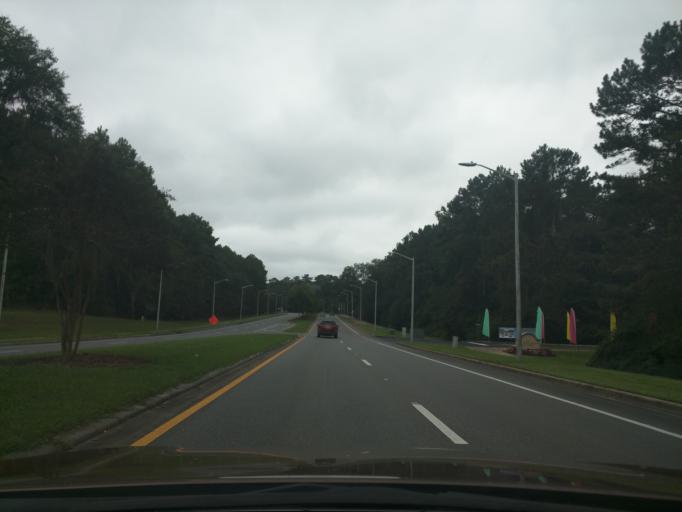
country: US
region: Florida
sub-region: Leon County
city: Tallahassee
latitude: 30.4325
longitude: -84.2017
